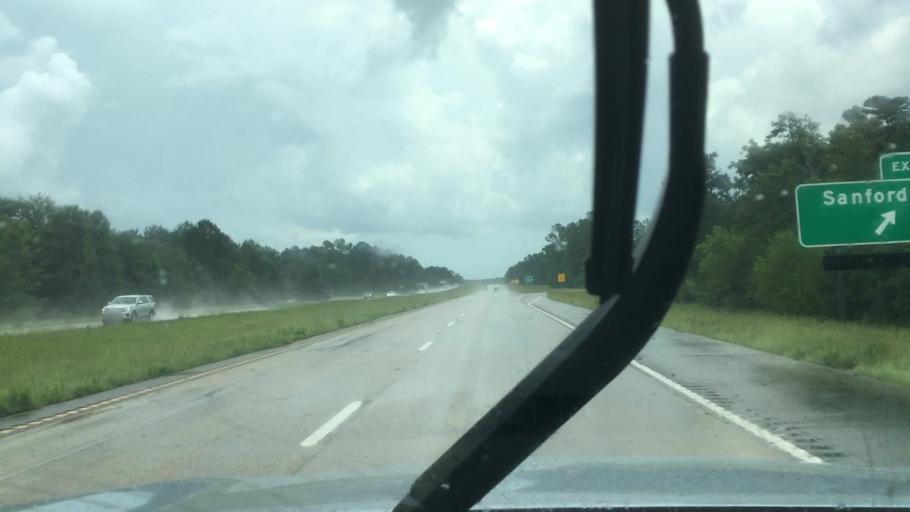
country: US
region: Mississippi
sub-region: Forrest County
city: Rawls Springs
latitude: 31.4955
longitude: -89.3161
